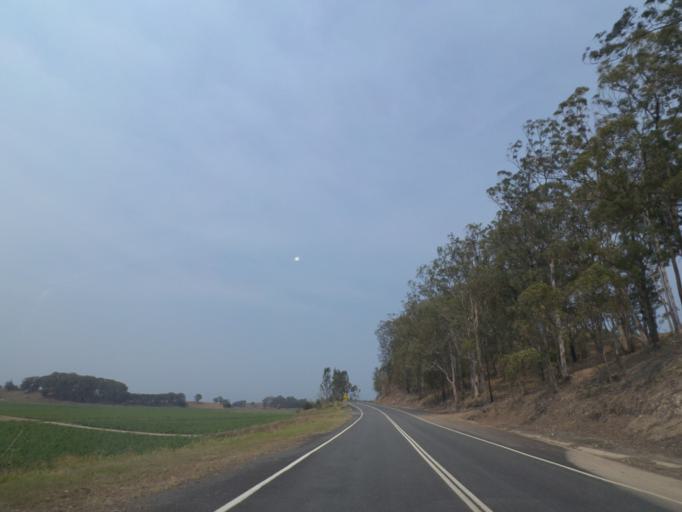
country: AU
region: New South Wales
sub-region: Tweed
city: Burringbar
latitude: -28.4584
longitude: 153.5198
